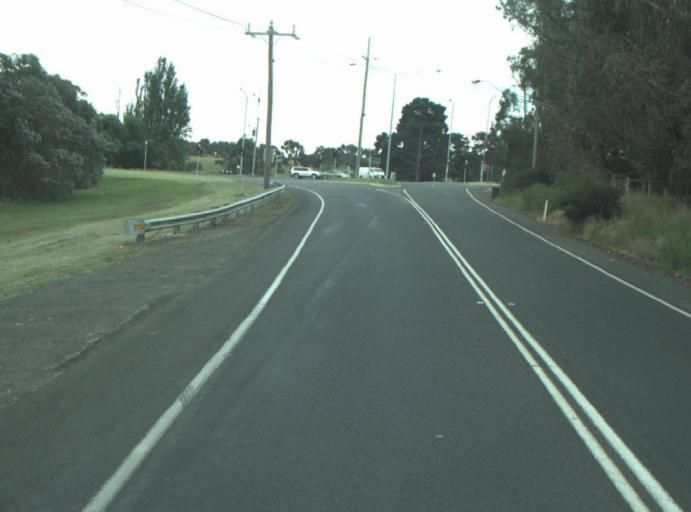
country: AU
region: Victoria
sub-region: Greater Geelong
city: Leopold
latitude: -38.2104
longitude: 144.5092
